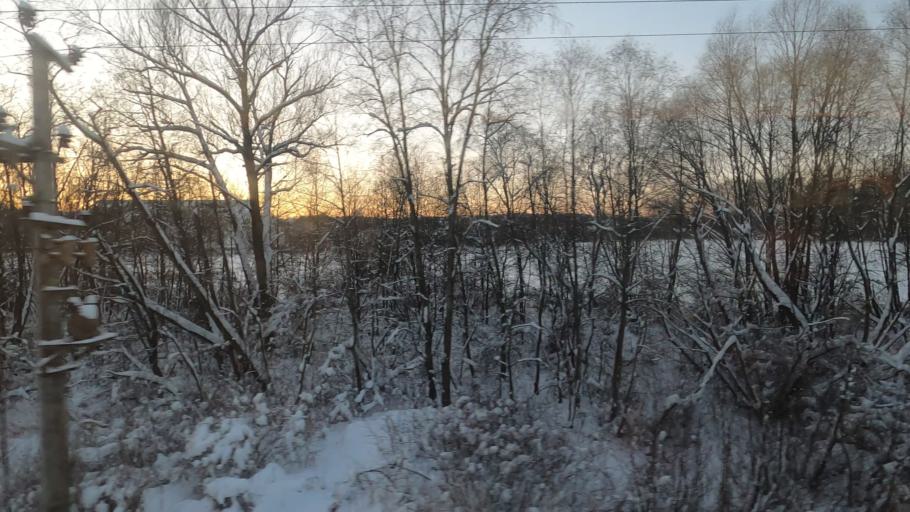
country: RU
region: Moskovskaya
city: Podosinki
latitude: 56.2099
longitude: 37.5264
